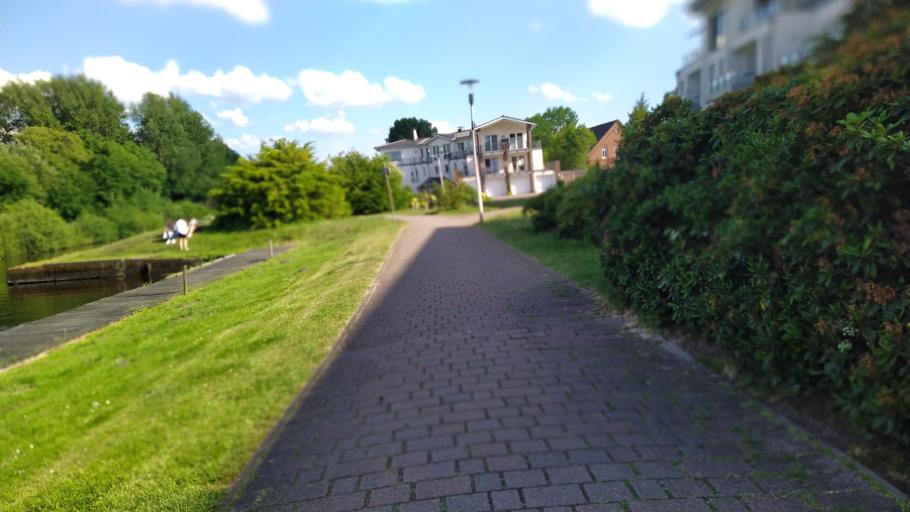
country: DE
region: Lower Saxony
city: Lintig
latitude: 53.6261
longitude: 8.8453
